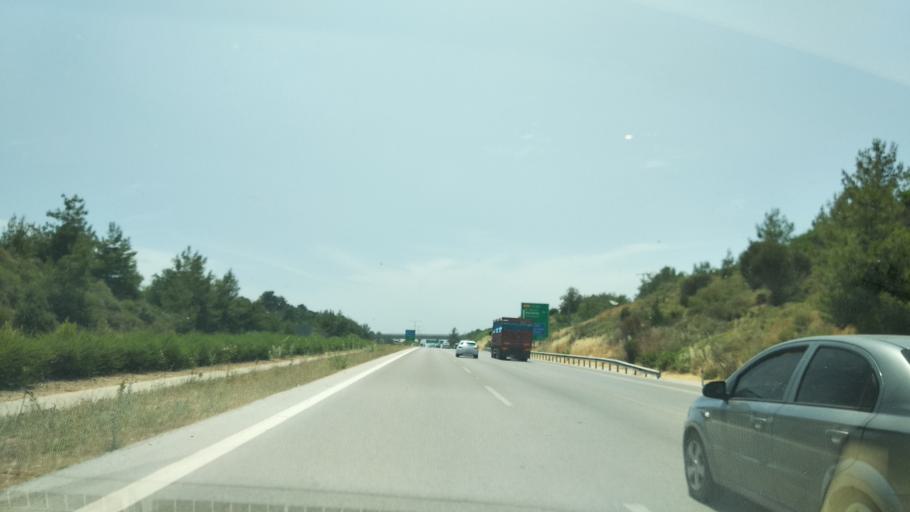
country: TR
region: Mersin
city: Mezitli
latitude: 36.7760
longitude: 34.4883
